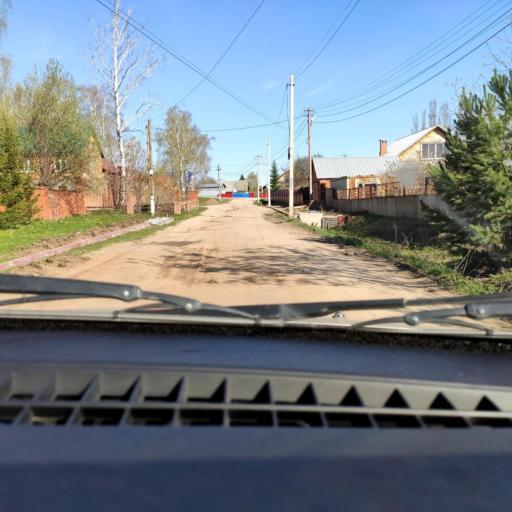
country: RU
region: Bashkortostan
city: Kabakovo
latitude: 54.5937
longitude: 56.1754
